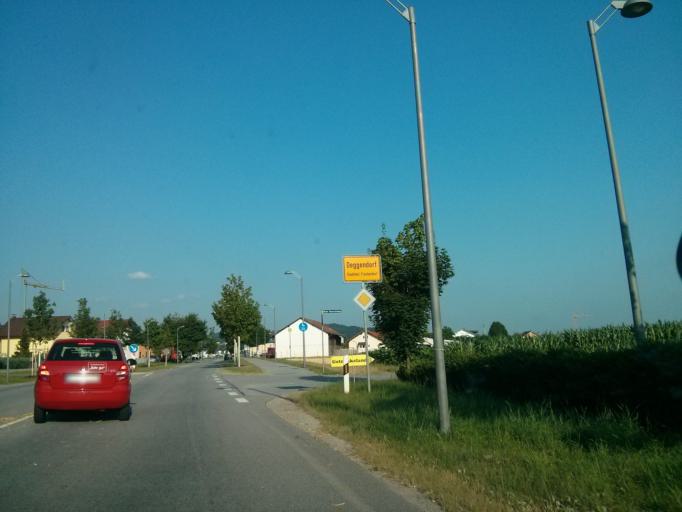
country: DE
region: Bavaria
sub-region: Lower Bavaria
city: Deggendorf
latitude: 48.8228
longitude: 12.9454
